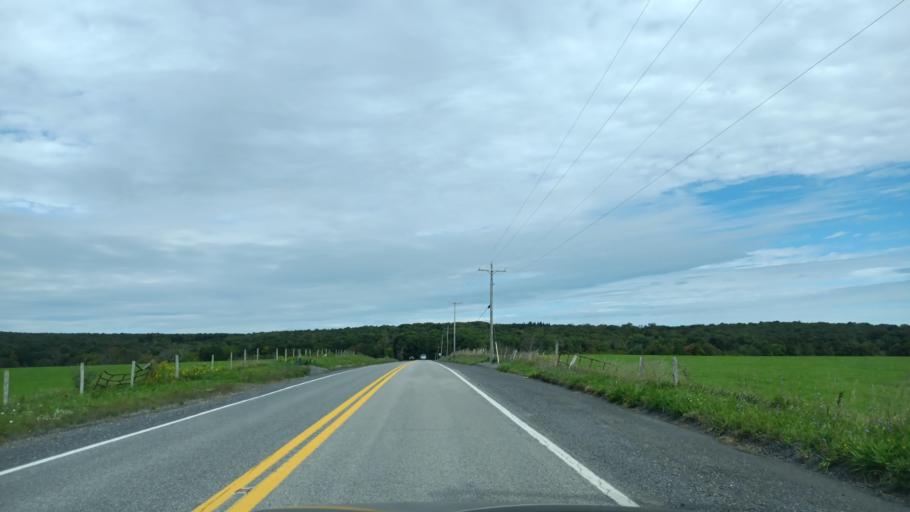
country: US
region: Maryland
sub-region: Garrett County
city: Mountain Lake Park
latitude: 39.2386
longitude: -79.2209
